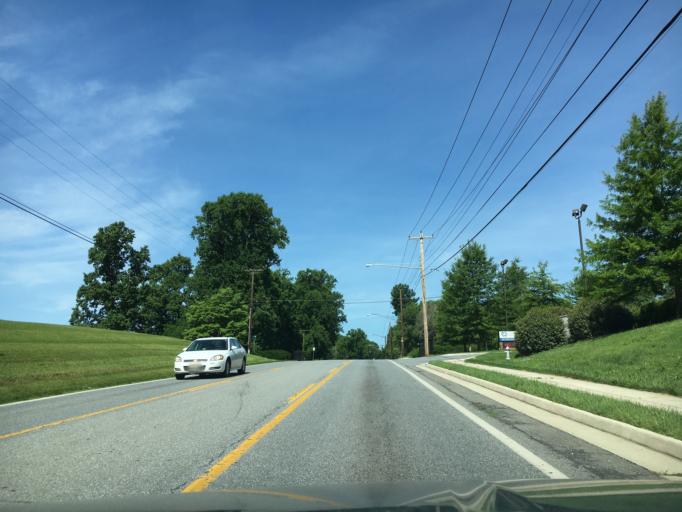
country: US
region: Virginia
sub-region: City of Lynchburg
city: West Lynchburg
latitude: 37.4018
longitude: -79.1887
